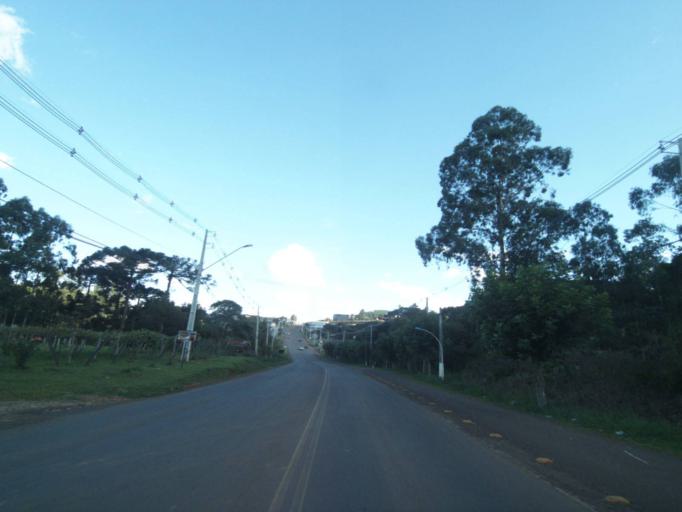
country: BR
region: Parana
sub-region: Uniao Da Vitoria
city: Uniao da Vitoria
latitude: -26.1580
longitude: -51.5412
